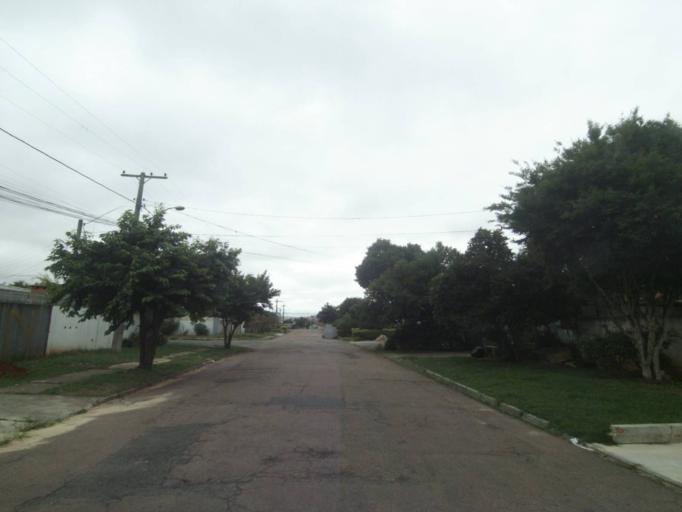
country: BR
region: Parana
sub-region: Sao Jose Dos Pinhais
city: Sao Jose dos Pinhais
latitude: -25.5461
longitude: -49.2787
